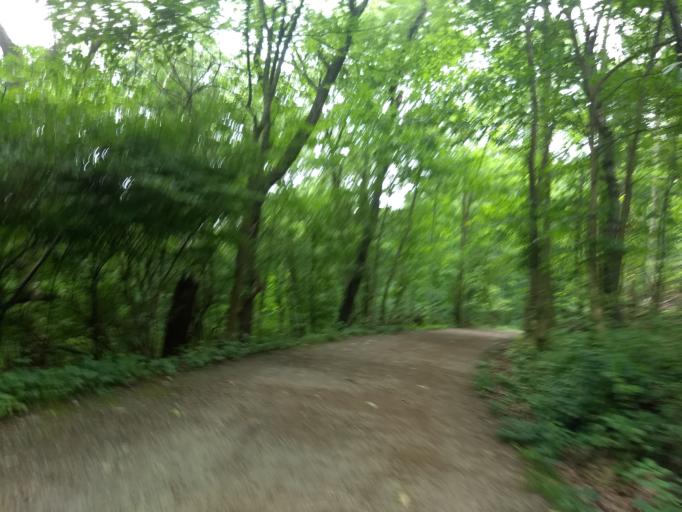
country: US
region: Pennsylvania
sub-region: Allegheny County
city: Edgewood
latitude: 40.4357
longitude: -79.9028
